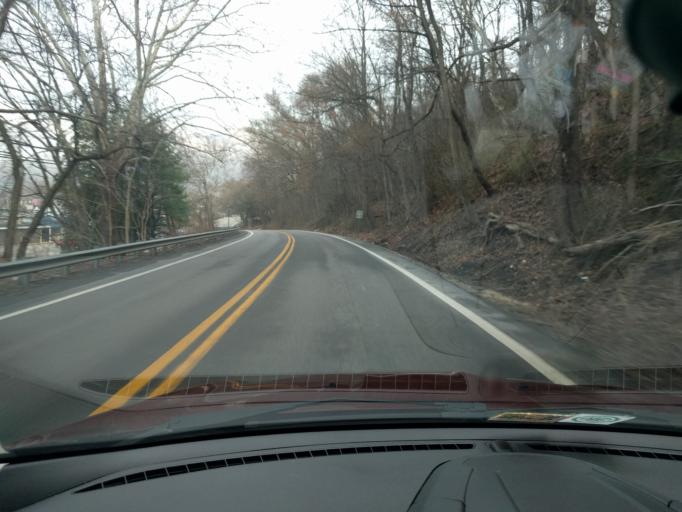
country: US
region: West Virginia
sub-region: Kanawha County
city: Montgomery
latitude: 38.1697
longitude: -81.3029
